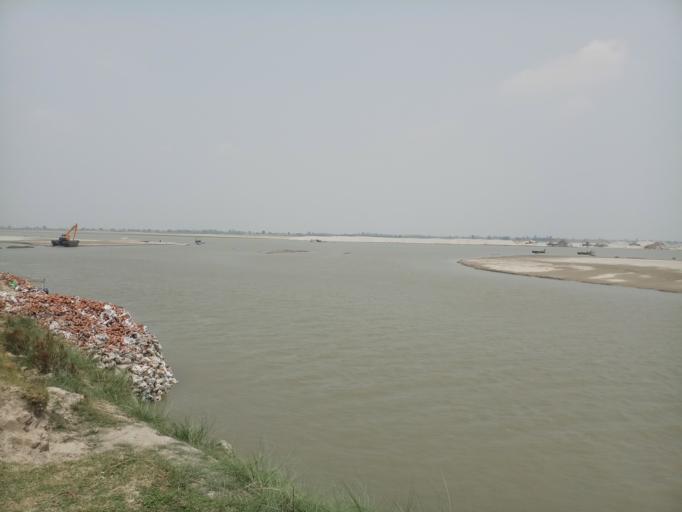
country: IN
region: Uttar Pradesh
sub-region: Bara Banki
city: Tikaitnagar
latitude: 27.0258
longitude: 81.5548
